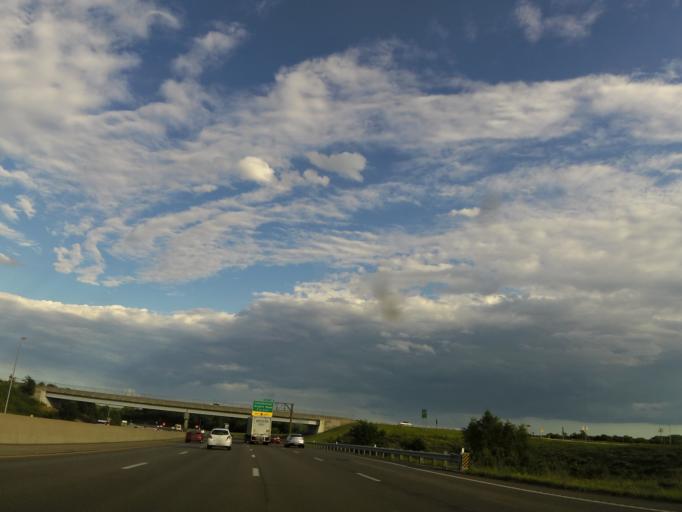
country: US
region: Missouri
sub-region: Saint Charles County
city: Weldon Spring
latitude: 38.7041
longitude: -90.6743
